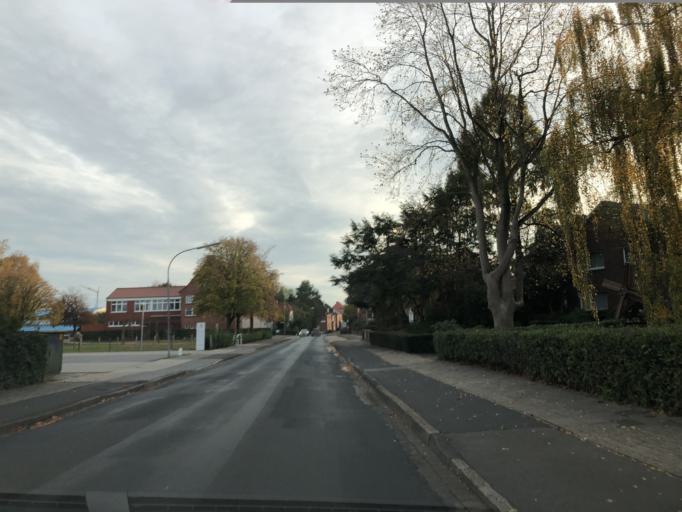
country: DE
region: Lower Saxony
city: Lehe
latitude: 53.0564
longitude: 7.3353
